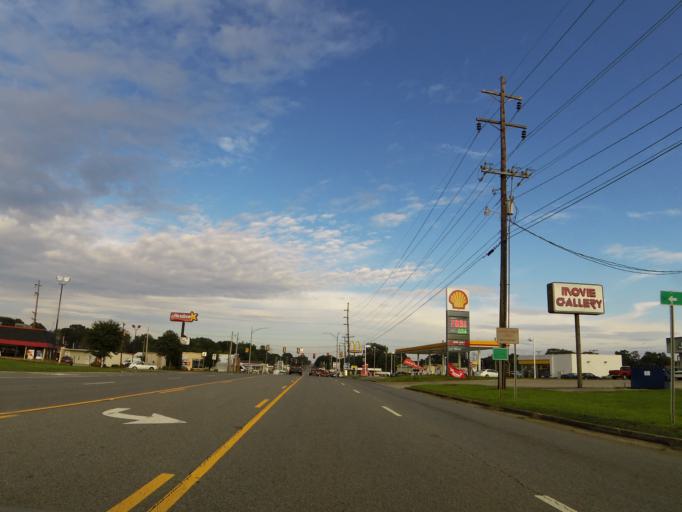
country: US
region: Alabama
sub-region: Lauderdale County
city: Rogersville
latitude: 34.8246
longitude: -87.2958
